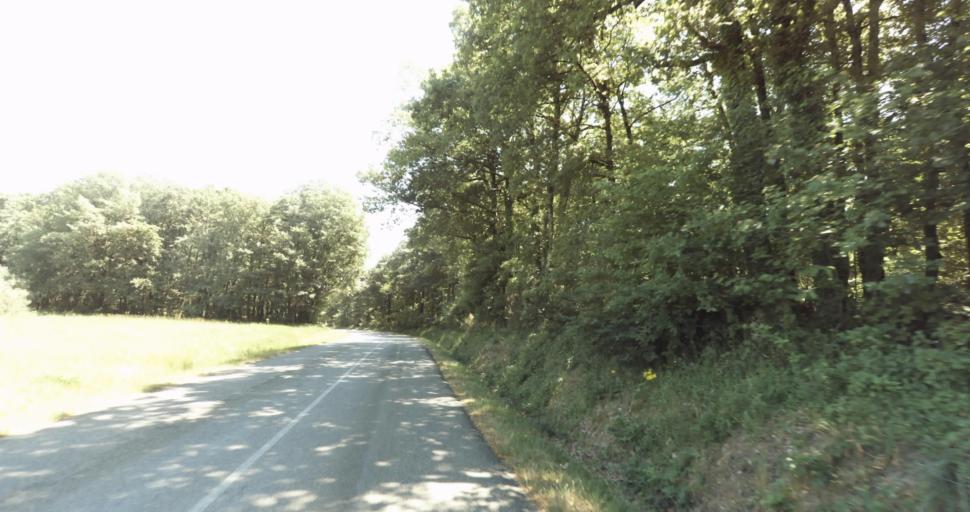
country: FR
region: Midi-Pyrenees
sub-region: Departement de la Haute-Garonne
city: Levignac
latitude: 43.6243
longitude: 1.1866
